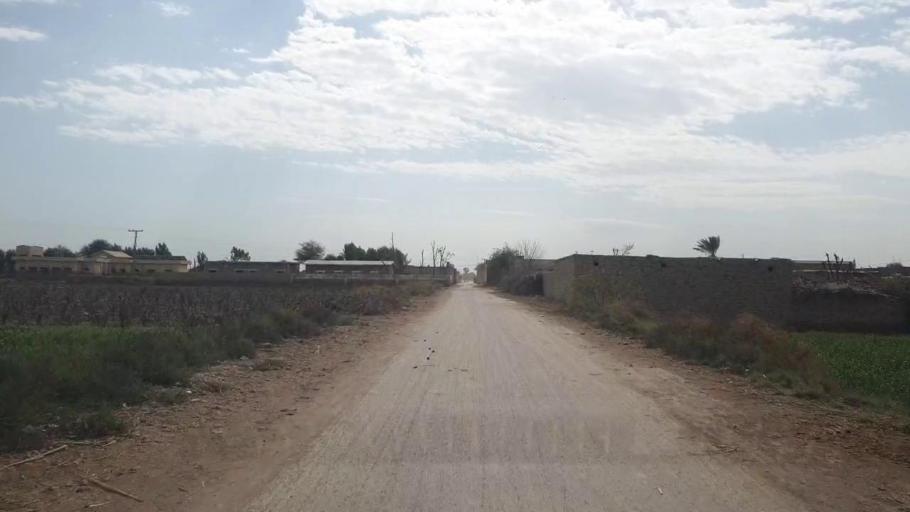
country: PK
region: Sindh
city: Hala
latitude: 25.9434
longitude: 68.4298
